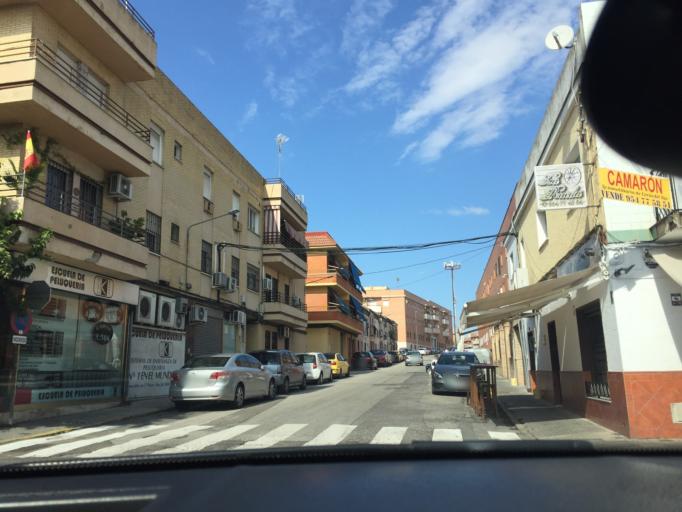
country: ES
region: Andalusia
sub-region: Provincia de Sevilla
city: Coria del Rio
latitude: 37.2940
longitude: -6.0519
